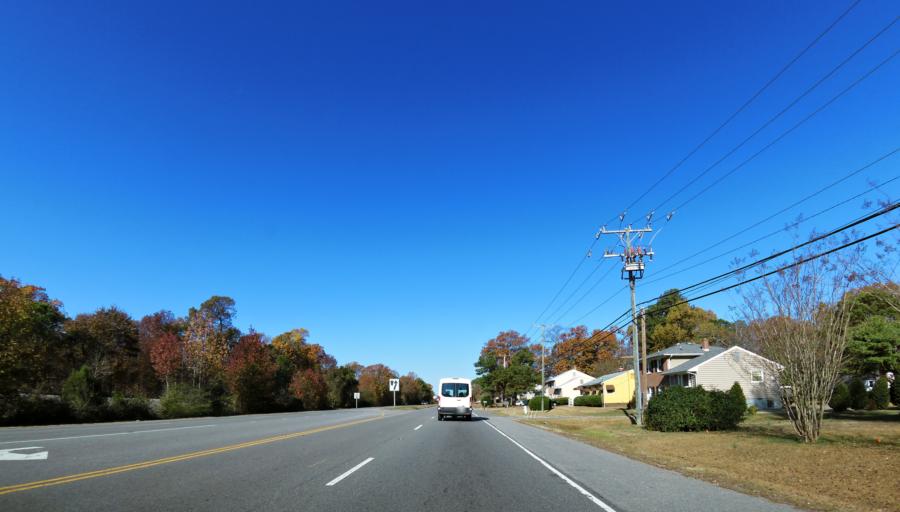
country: US
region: Virginia
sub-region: City of Williamsburg
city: Williamsburg
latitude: 37.2483
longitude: -76.6574
